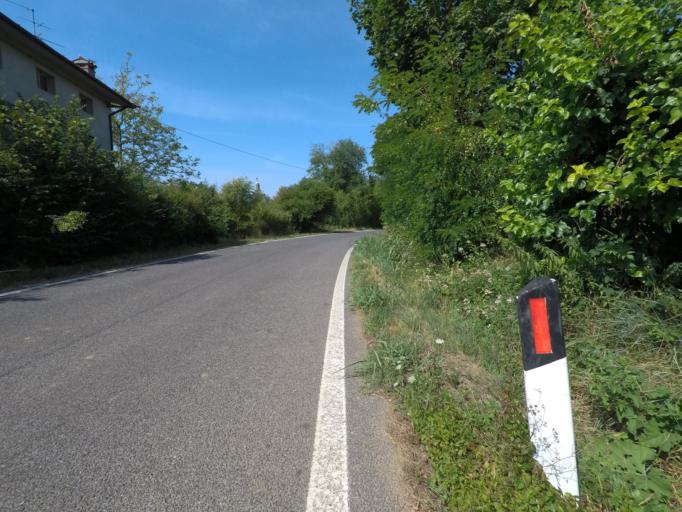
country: IT
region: Friuli Venezia Giulia
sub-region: Provincia di Udine
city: Mereto di Tomba
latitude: 46.0700
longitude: 13.0289
